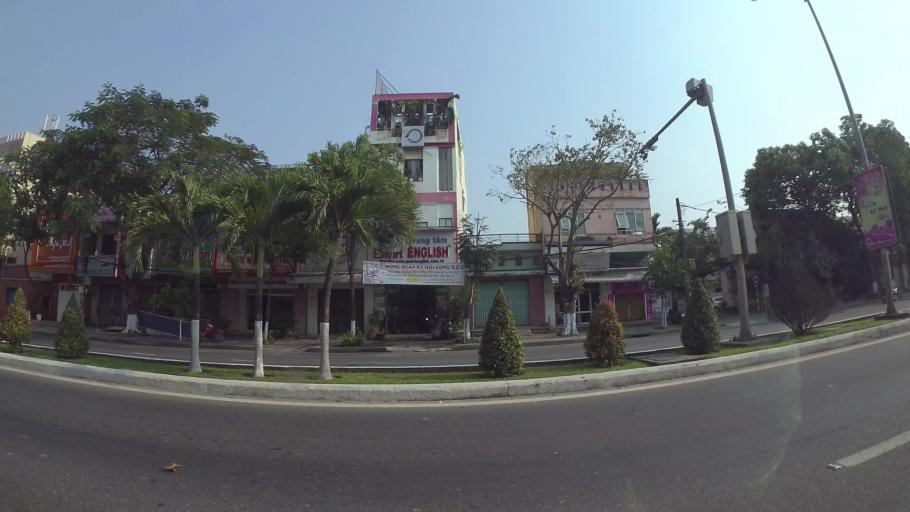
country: VN
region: Da Nang
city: Cam Le
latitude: 16.0191
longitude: 108.2087
